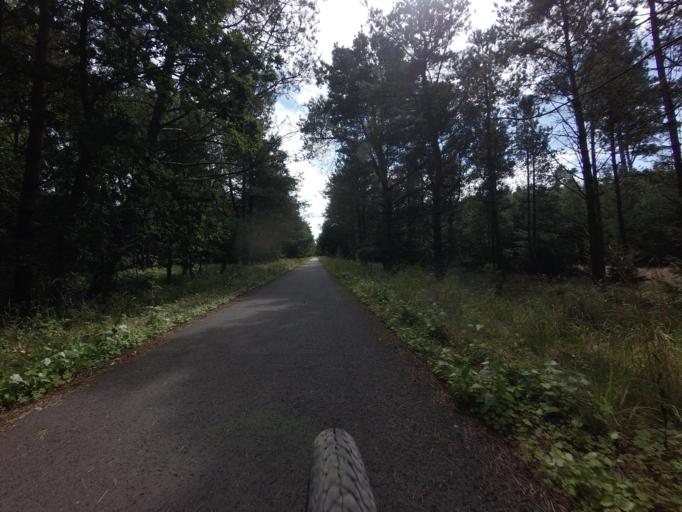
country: DK
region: Central Jutland
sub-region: Norddjurs Kommune
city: Auning
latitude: 56.4067
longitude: 10.3975
